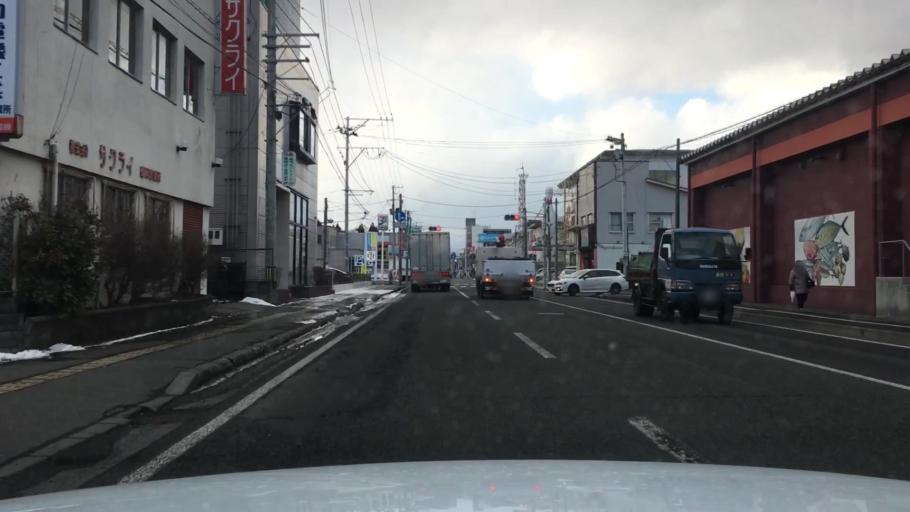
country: JP
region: Iwate
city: Morioka-shi
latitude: 39.6921
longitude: 141.1720
